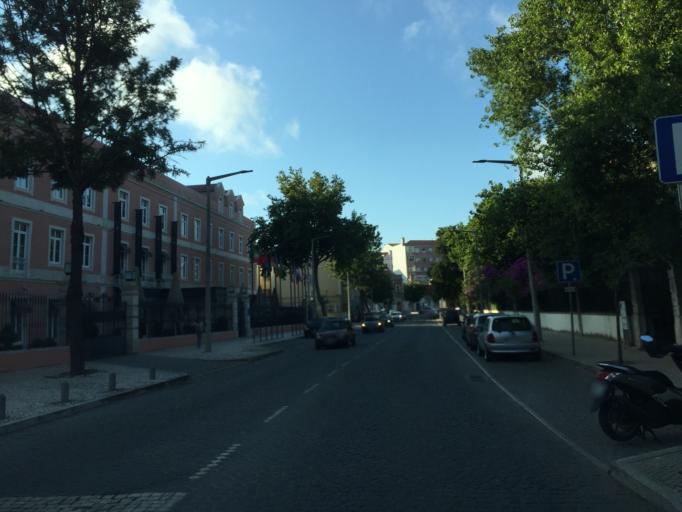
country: PT
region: Leiria
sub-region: Caldas da Rainha
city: Caldas da Rainha
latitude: 39.4009
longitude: -9.1360
